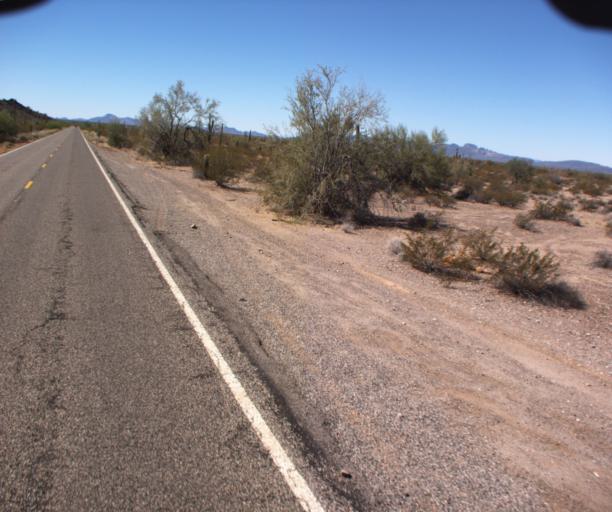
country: US
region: Arizona
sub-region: Pima County
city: Ajo
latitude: 32.2359
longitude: -112.7515
